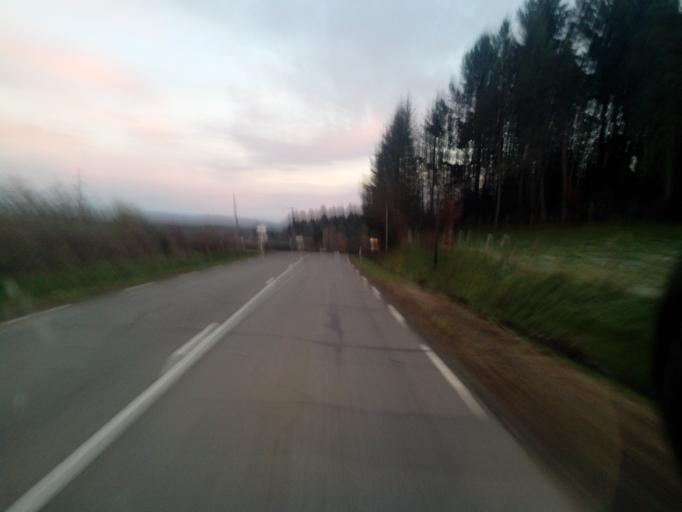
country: FR
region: Limousin
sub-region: Departement de la Correze
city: Meymac
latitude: 45.5176
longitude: 2.1741
